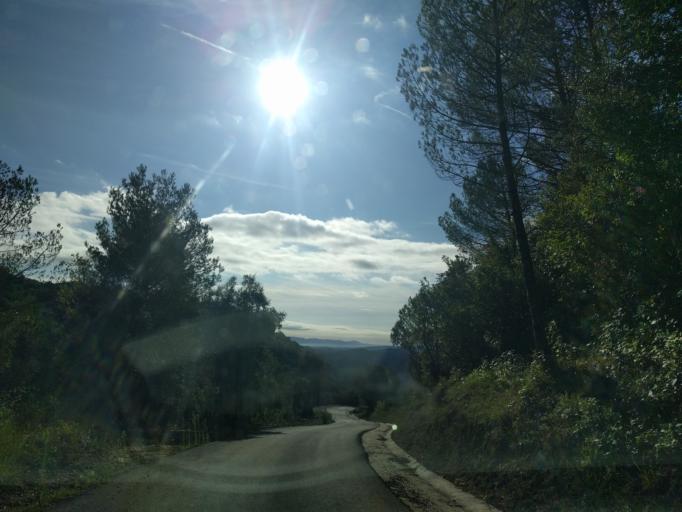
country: ES
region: Catalonia
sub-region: Provincia de Girona
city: la Cellera de Ter
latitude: 42.0140
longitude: 2.6312
